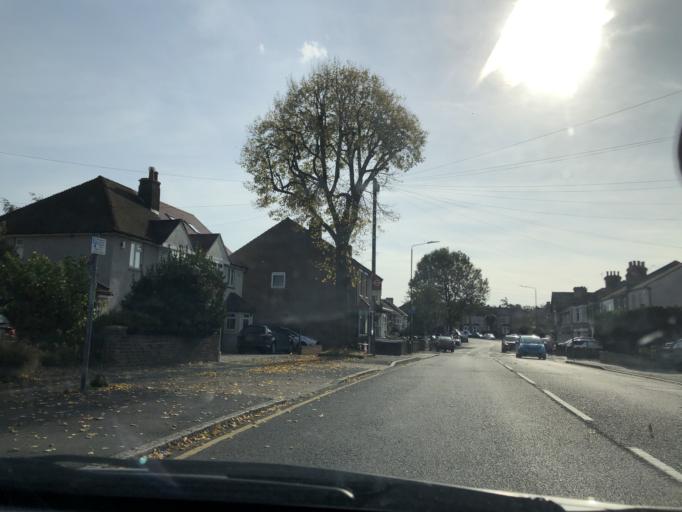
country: GB
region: England
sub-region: Greater London
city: Bexley
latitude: 51.4467
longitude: 0.1804
